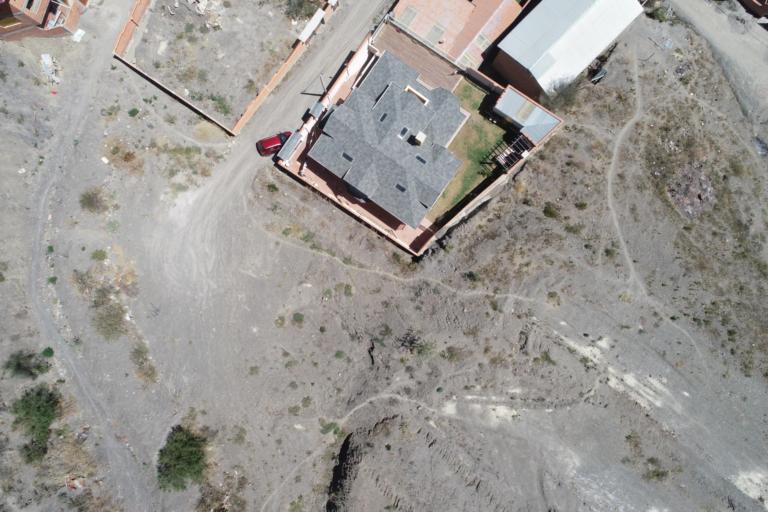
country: BO
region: La Paz
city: La Paz
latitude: -16.6263
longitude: -68.0509
